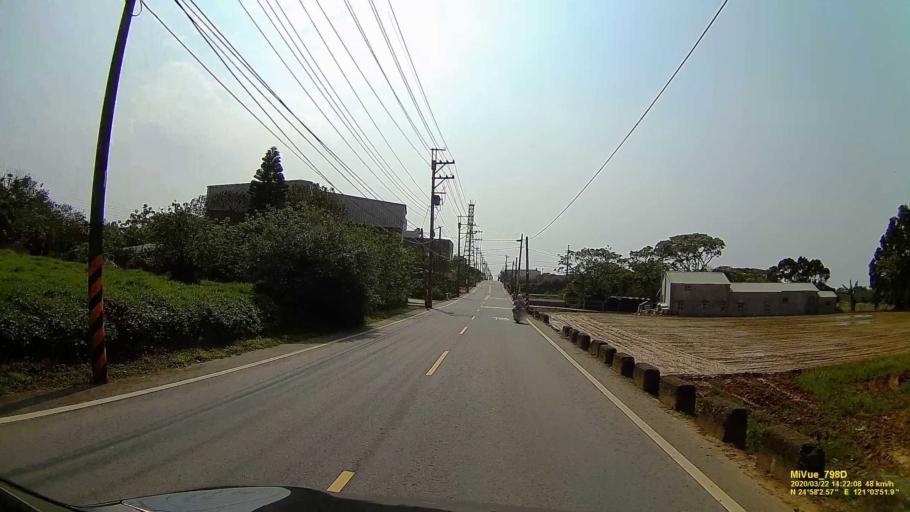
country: TW
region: Taiwan
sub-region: Hsinchu
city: Zhubei
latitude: 24.9673
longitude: 121.0642
